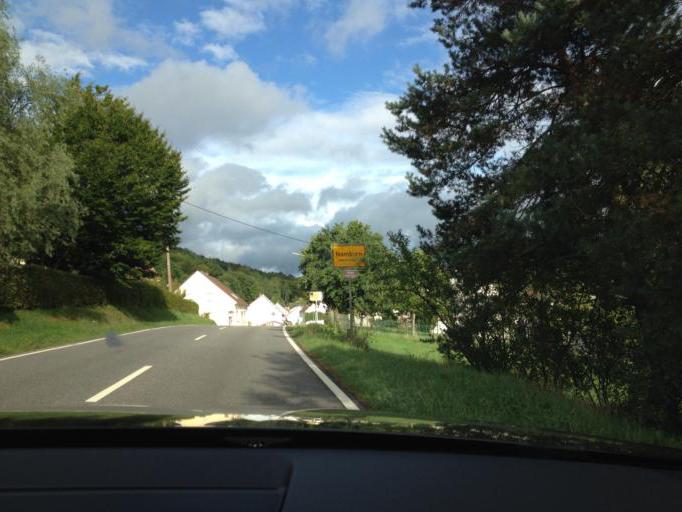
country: DE
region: Saarland
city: Namborn
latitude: 49.5227
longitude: 7.1308
